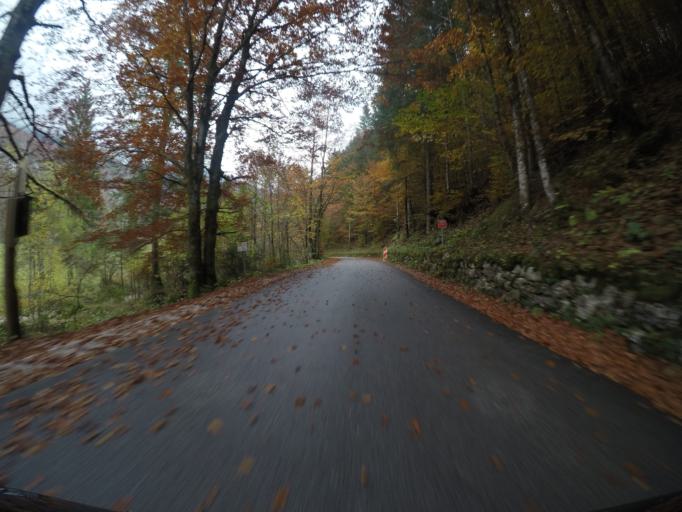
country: SI
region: Jesenice
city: Hrusica
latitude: 46.4189
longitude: 13.9822
